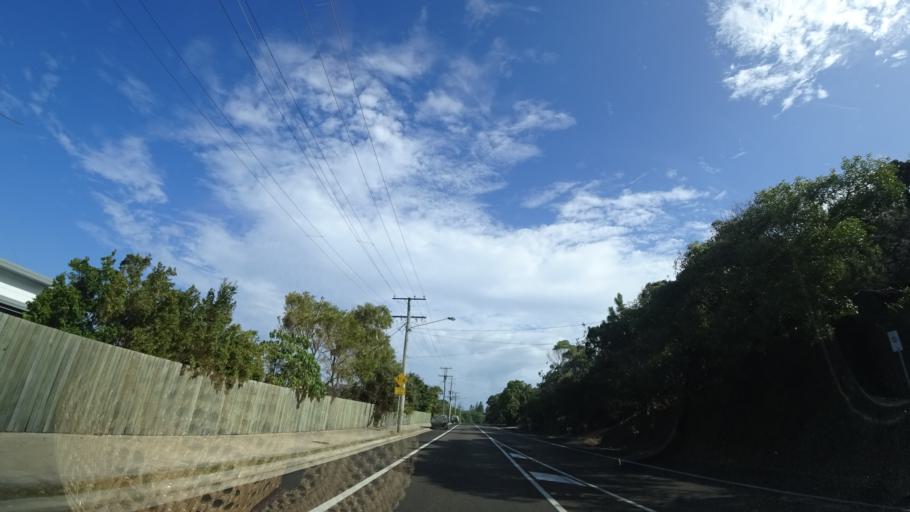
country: AU
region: Queensland
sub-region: Sunshine Coast
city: Coolum Beach
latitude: -26.5462
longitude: 153.0995
